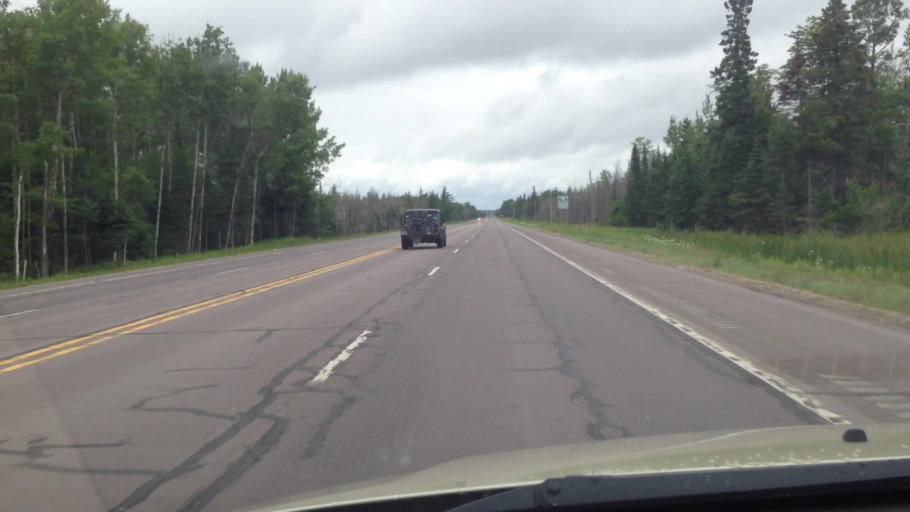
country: US
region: Michigan
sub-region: Schoolcraft County
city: Manistique
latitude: 46.0172
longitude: -85.9902
